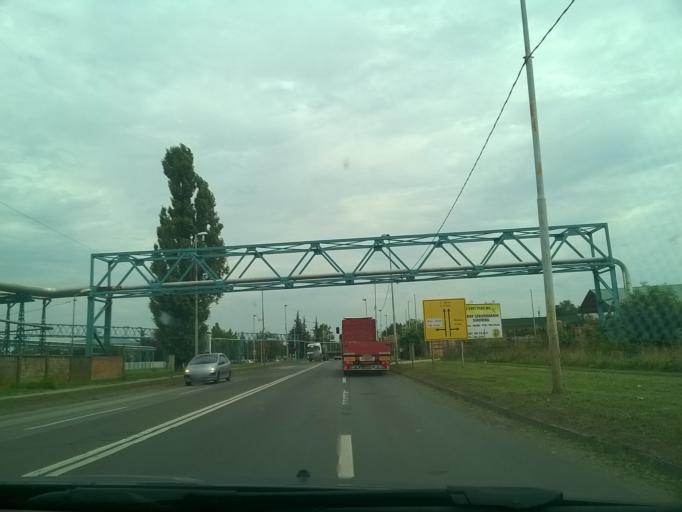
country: RS
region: Autonomna Pokrajina Vojvodina
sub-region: Srednjebanatski Okrug
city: Zrenjanin
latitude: 45.3870
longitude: 20.4208
